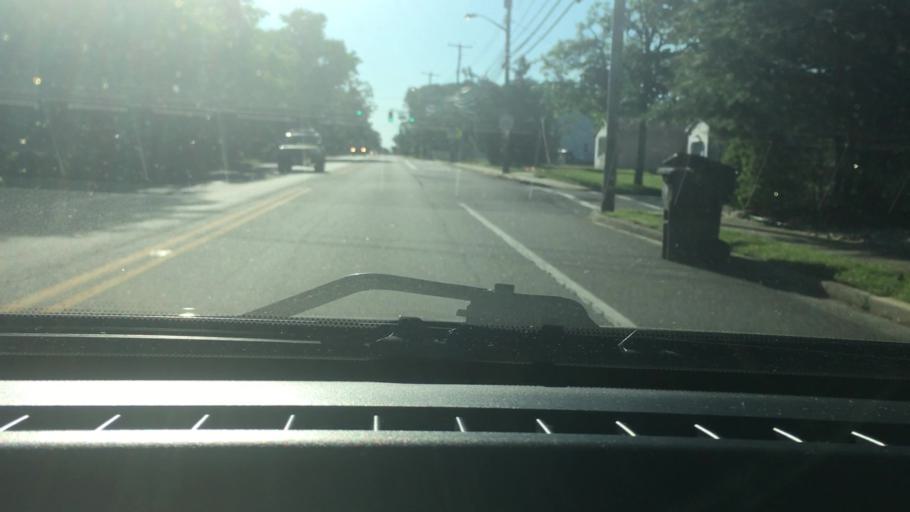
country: US
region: New Jersey
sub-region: Ocean County
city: Island Heights
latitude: 39.9699
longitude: -74.1455
